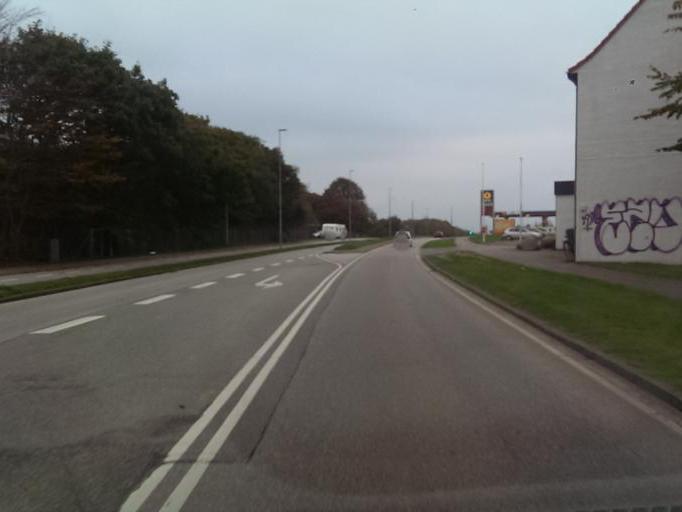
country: DK
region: South Denmark
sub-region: Esbjerg Kommune
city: Esbjerg
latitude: 55.4634
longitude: 8.4660
